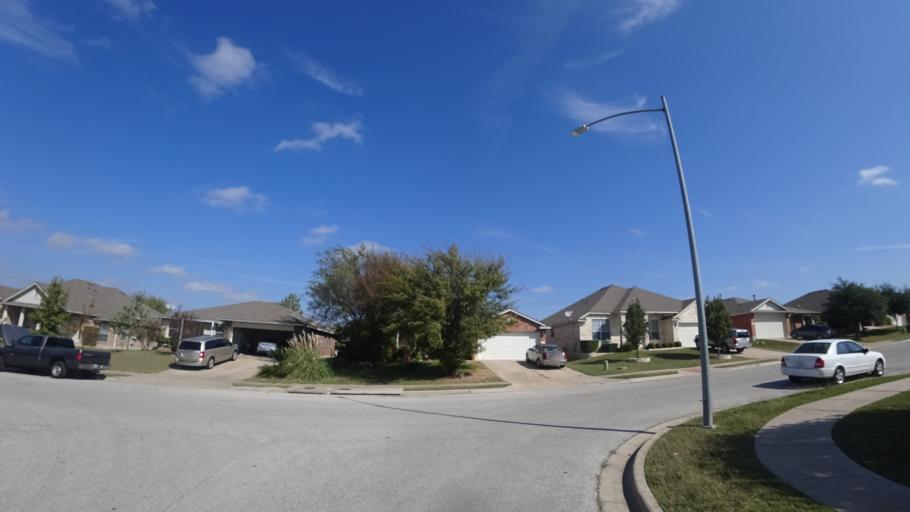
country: US
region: Texas
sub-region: Travis County
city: Pflugerville
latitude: 30.4211
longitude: -97.6354
